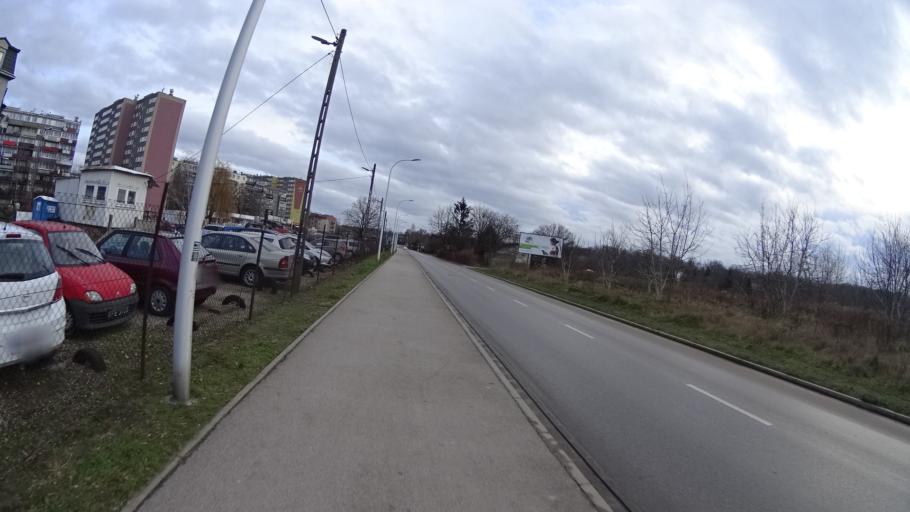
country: PL
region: Masovian Voivodeship
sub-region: Powiat pruszkowski
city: Granica
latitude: 52.1560
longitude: 20.7861
